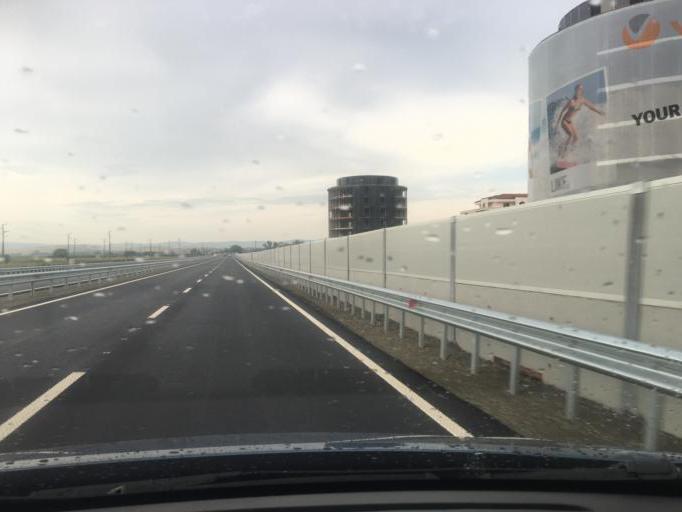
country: BG
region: Burgas
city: Aheloy
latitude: 42.6294
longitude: 27.6330
